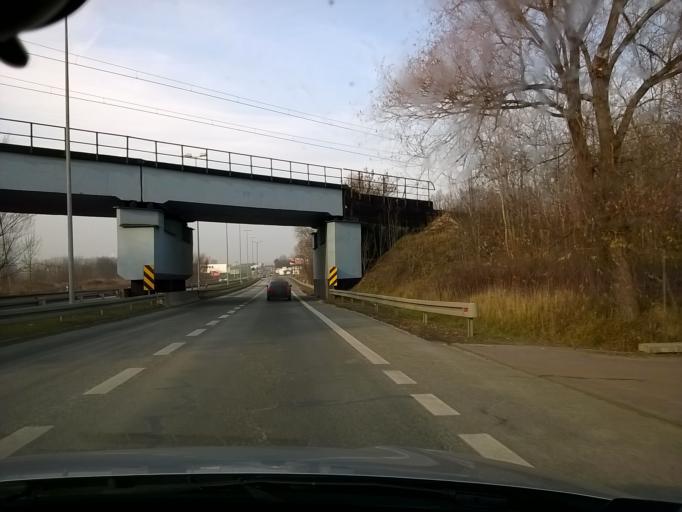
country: PL
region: Silesian Voivodeship
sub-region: Powiat gliwicki
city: Przyszowice
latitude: 50.2526
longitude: 18.7383
